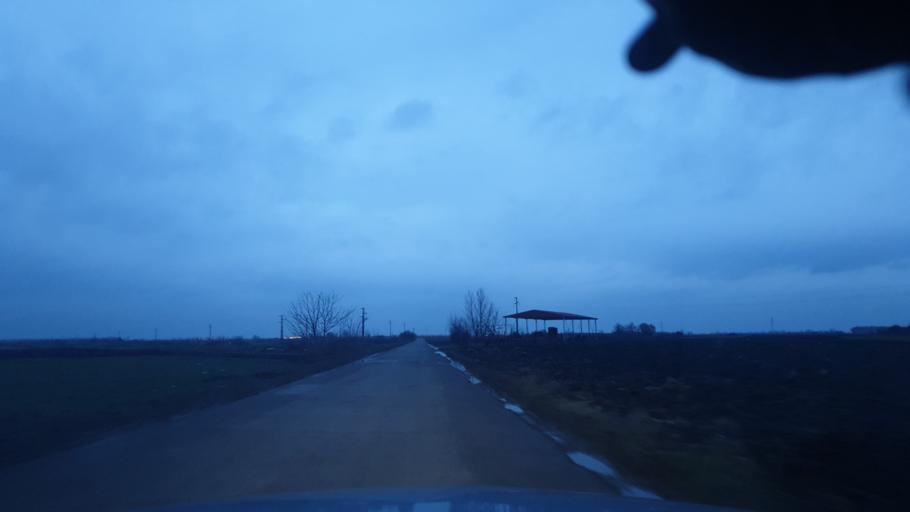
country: RS
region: Autonomna Pokrajina Vojvodina
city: Nova Pazova
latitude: 44.9332
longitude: 20.2142
